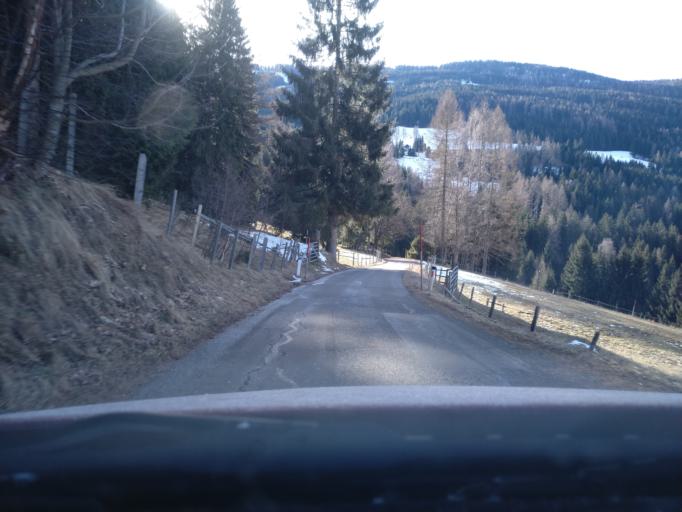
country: AT
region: Carinthia
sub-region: Politischer Bezirk Villach Land
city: Arriach
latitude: 46.7189
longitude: 13.8869
